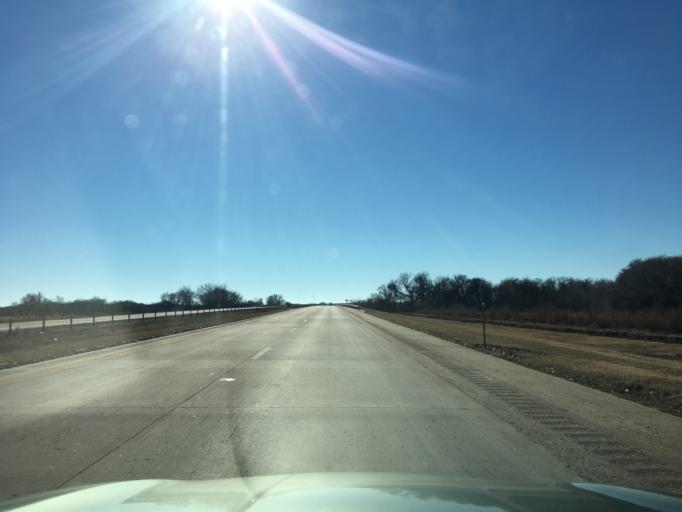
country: US
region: Oklahoma
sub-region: Kay County
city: Blackwell
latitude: 36.9111
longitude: -97.3524
